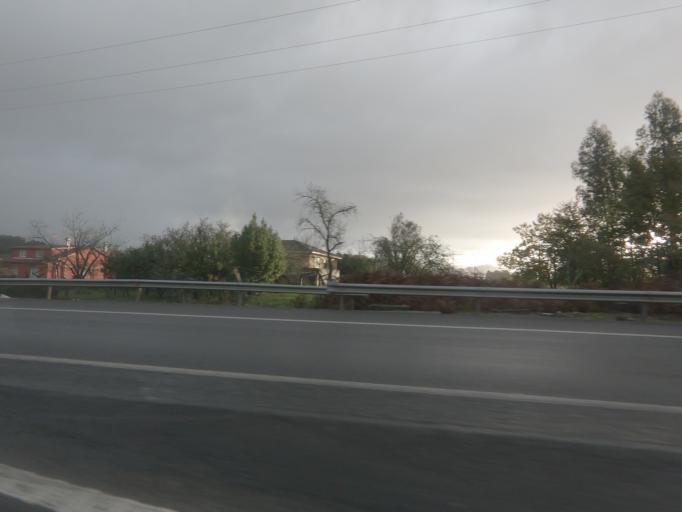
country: ES
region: Galicia
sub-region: Provincia de Pontevedra
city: Redondela
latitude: 42.2255
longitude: -8.6440
